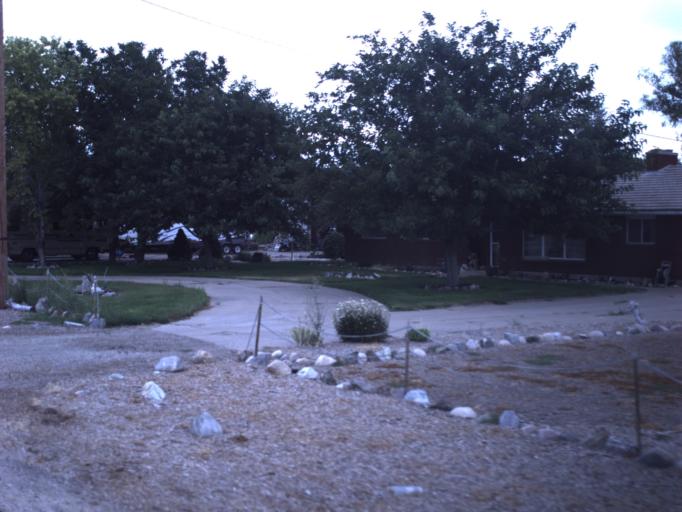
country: US
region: Utah
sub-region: Davis County
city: West Point
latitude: 41.1091
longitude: -112.1125
